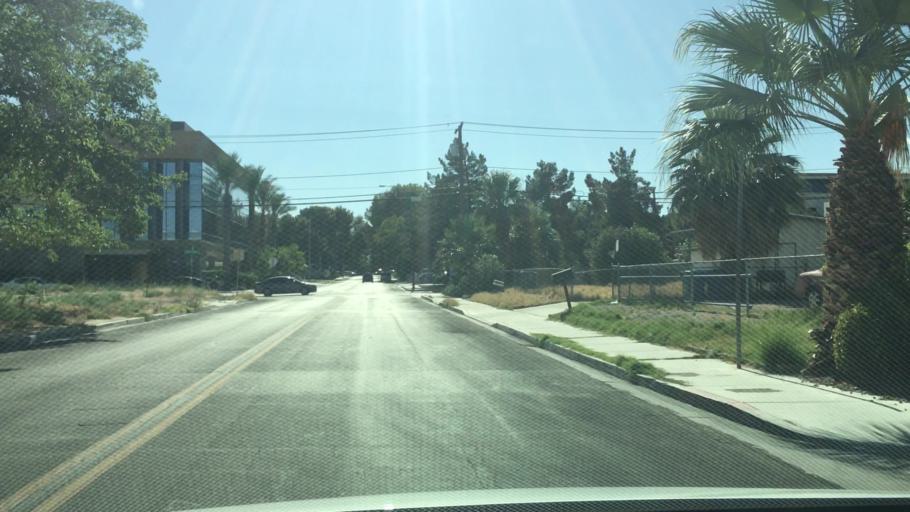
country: US
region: Nevada
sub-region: Clark County
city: Las Vegas
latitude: 36.1644
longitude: -115.1692
